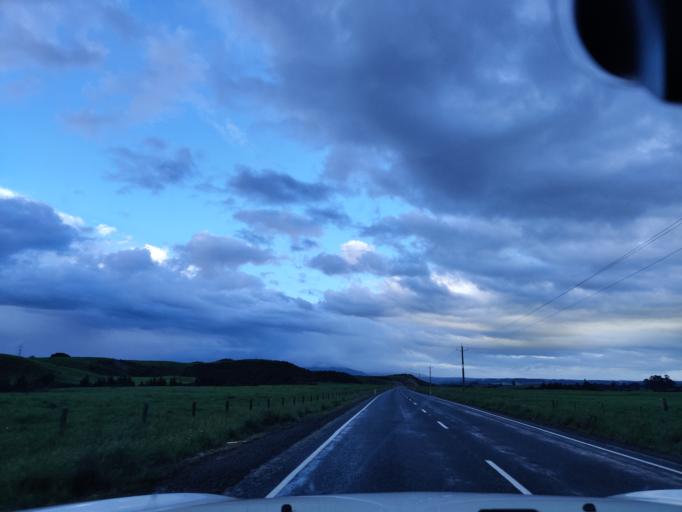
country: NZ
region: Waikato
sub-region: South Waikato District
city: Tokoroa
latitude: -38.3775
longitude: 175.7898
